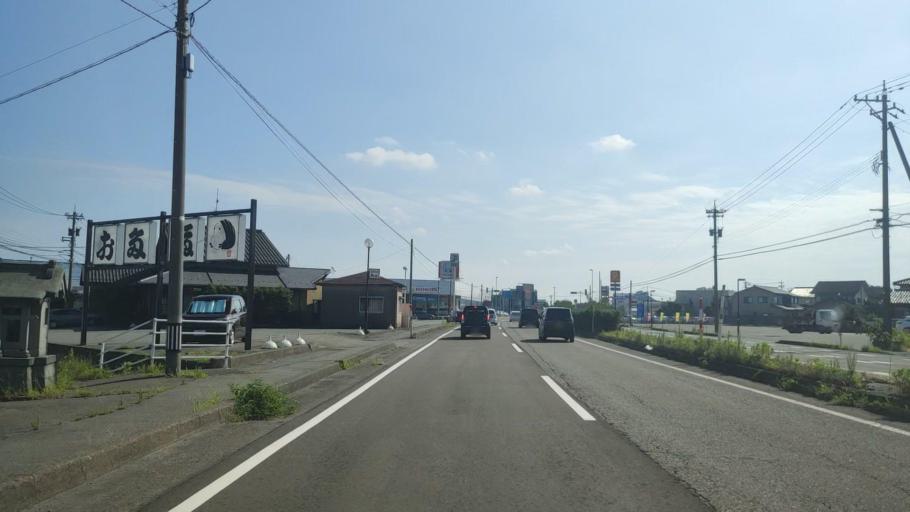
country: JP
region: Ishikawa
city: Matsuto
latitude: 36.5067
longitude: 136.5538
